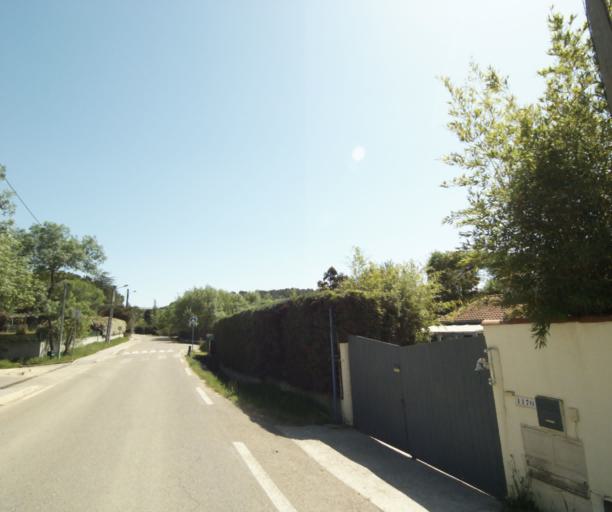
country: FR
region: Languedoc-Roussillon
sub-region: Departement de l'Herault
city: Prades-le-Lez
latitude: 43.6928
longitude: 3.8743
